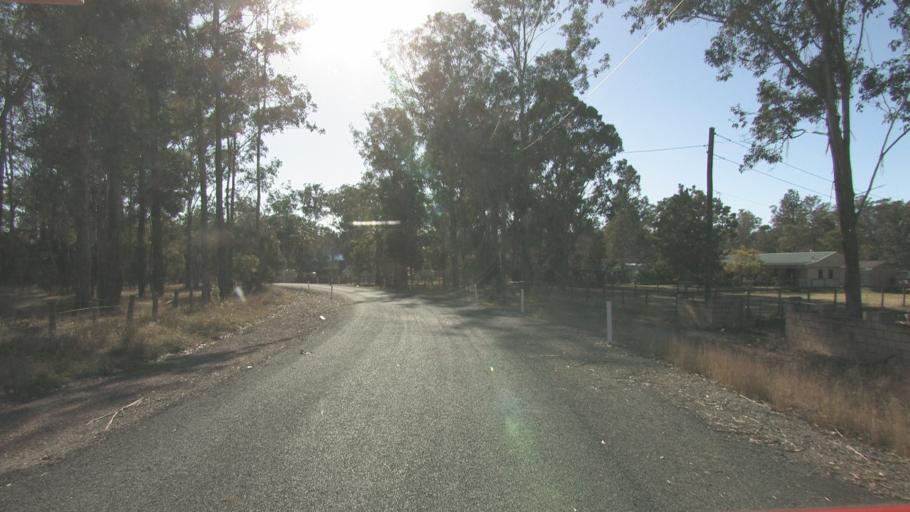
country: AU
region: Queensland
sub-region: Logan
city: Cedar Vale
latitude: -27.8427
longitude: 153.0020
